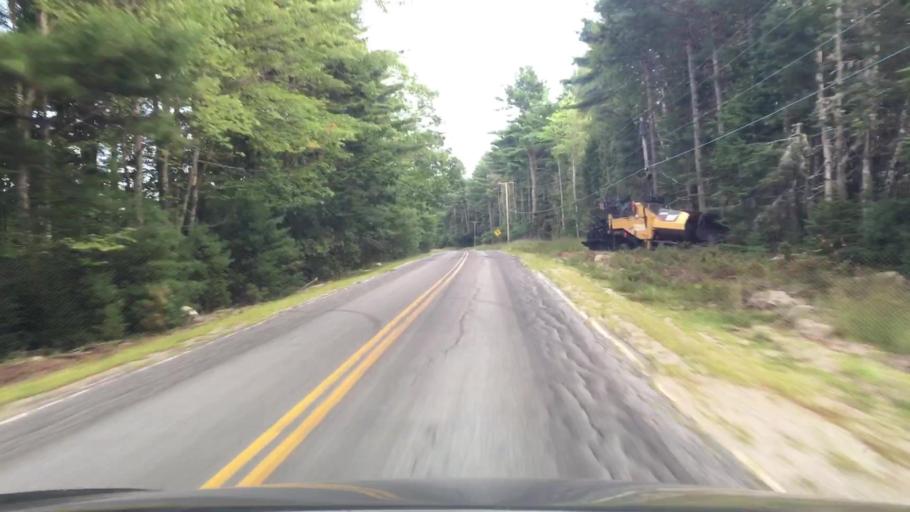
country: US
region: Maine
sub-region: Hancock County
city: Surry
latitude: 44.5097
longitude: -68.5981
